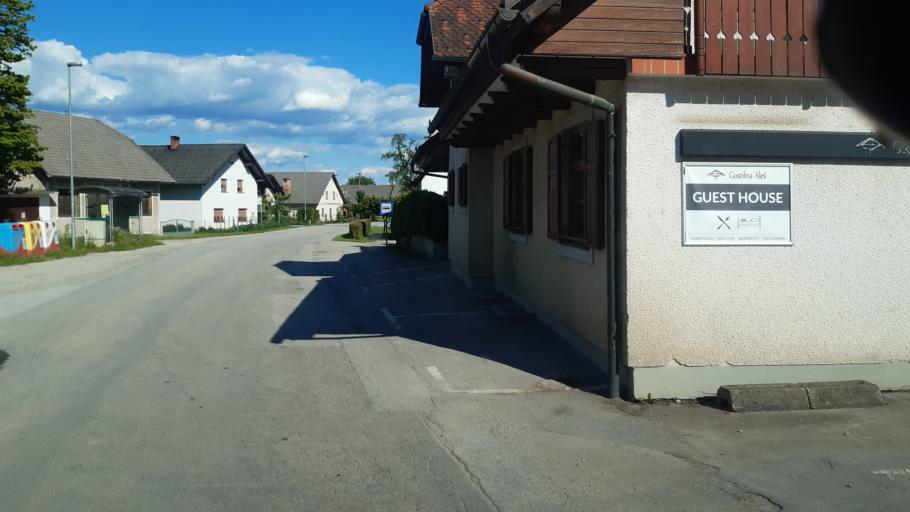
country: SI
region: Sencur
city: Hrastje
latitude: 46.2132
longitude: 14.3841
